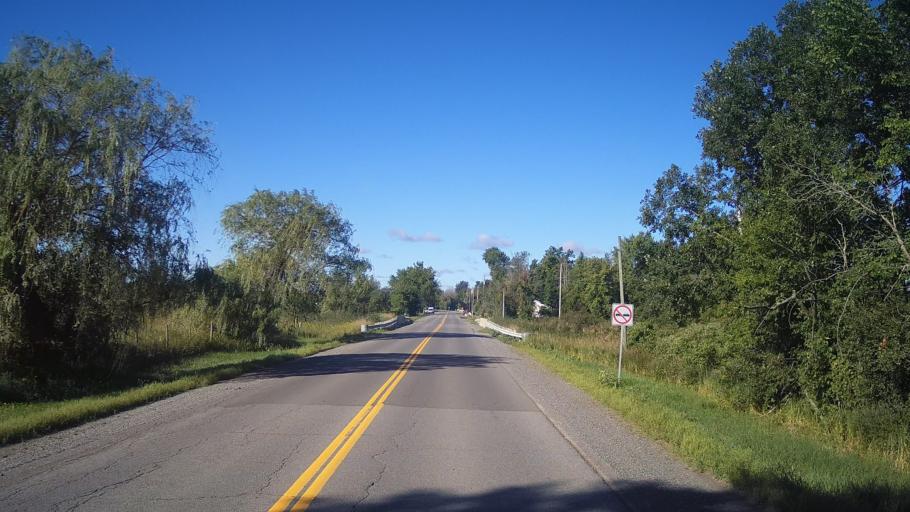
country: CA
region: Ontario
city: Bells Corners
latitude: 45.0939
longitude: -75.6204
